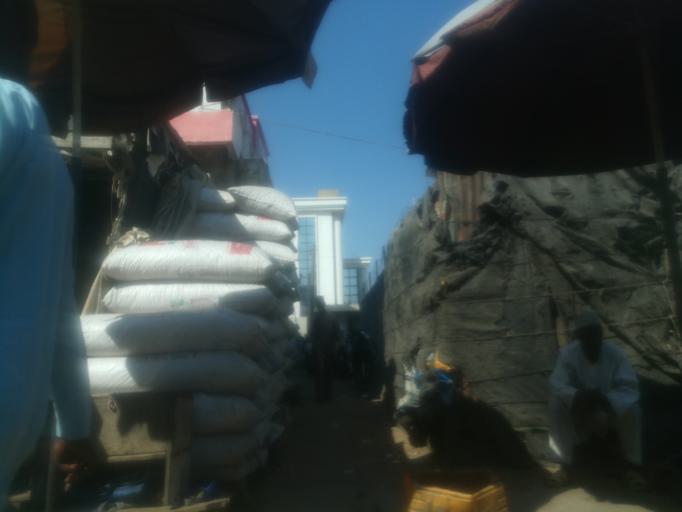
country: NG
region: Kano
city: Kano
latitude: 12.0103
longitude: 8.5352
